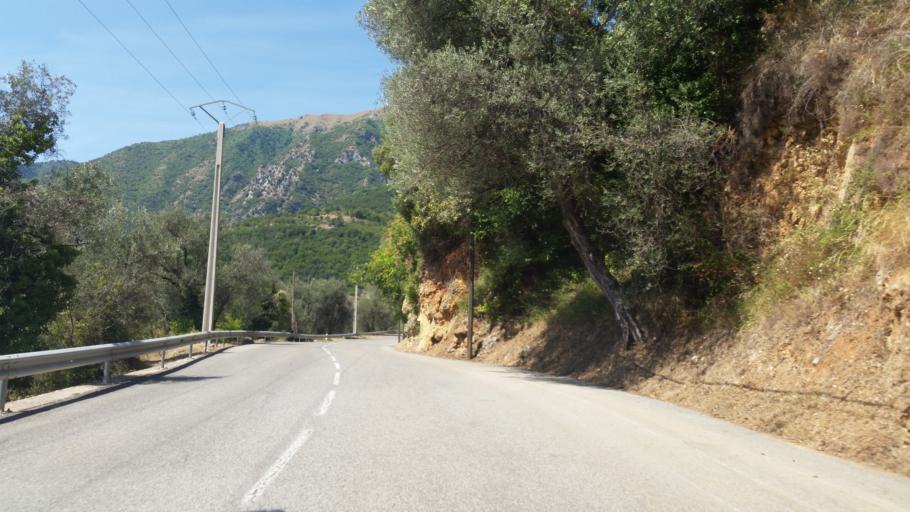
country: FR
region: Provence-Alpes-Cote d'Azur
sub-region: Departement des Alpes-Maritimes
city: Breil-sur-Roya
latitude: 43.9427
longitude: 7.5026
